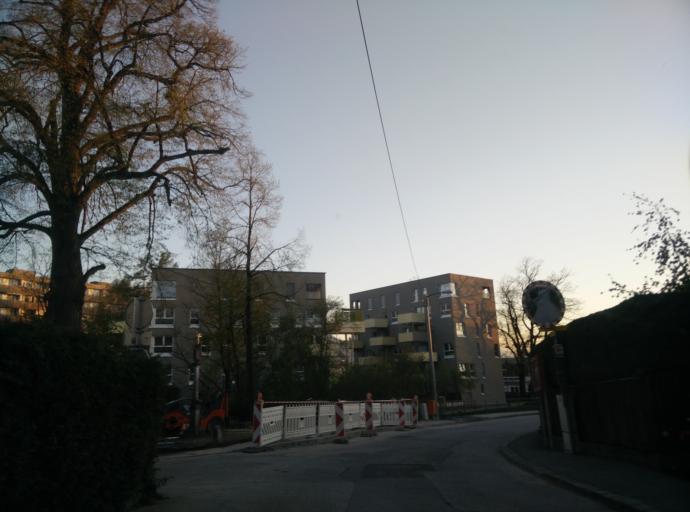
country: AT
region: Salzburg
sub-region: Politischer Bezirk Salzburg-Umgebung
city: Bergheim
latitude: 47.8280
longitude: 13.0387
